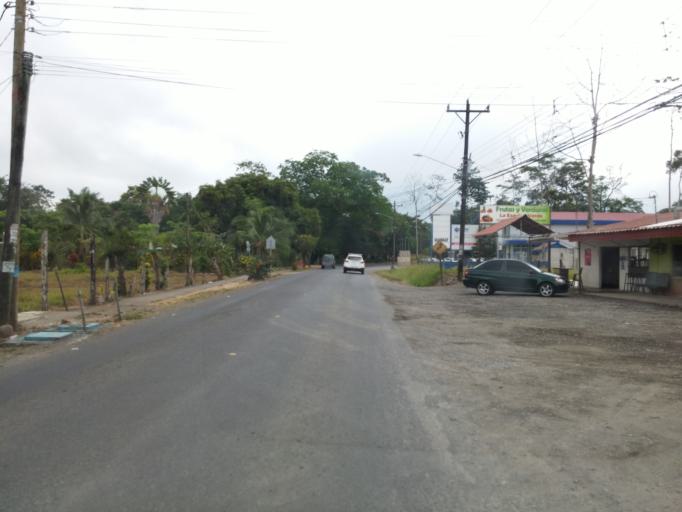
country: CR
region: Alajuela
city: Quesada
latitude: 10.3579
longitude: -84.5144
